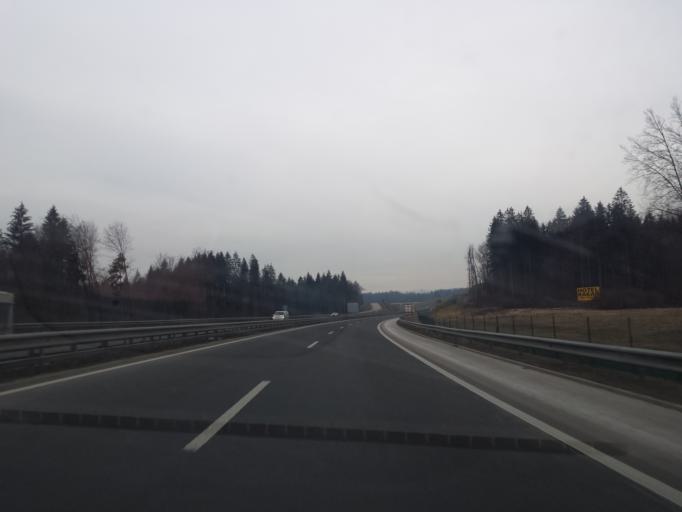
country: SI
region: Mirna Pec
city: Mirna Pec
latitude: 45.8920
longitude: 15.0598
